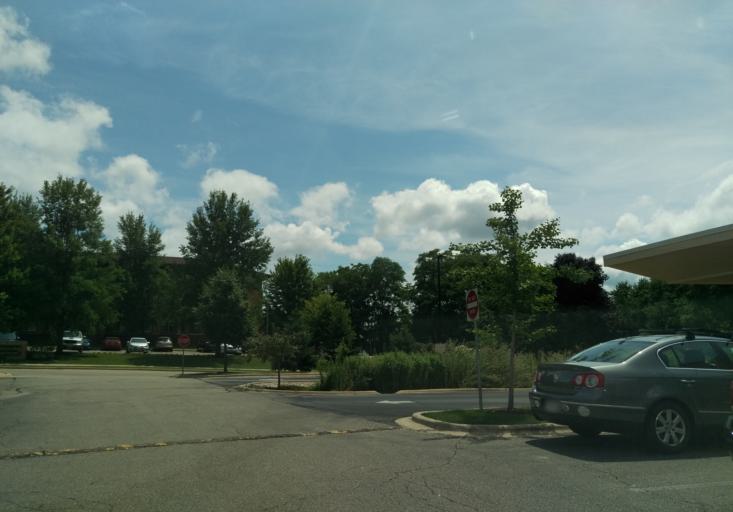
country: US
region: Wisconsin
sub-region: Dane County
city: Middleton
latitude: 43.1063
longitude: -89.4974
